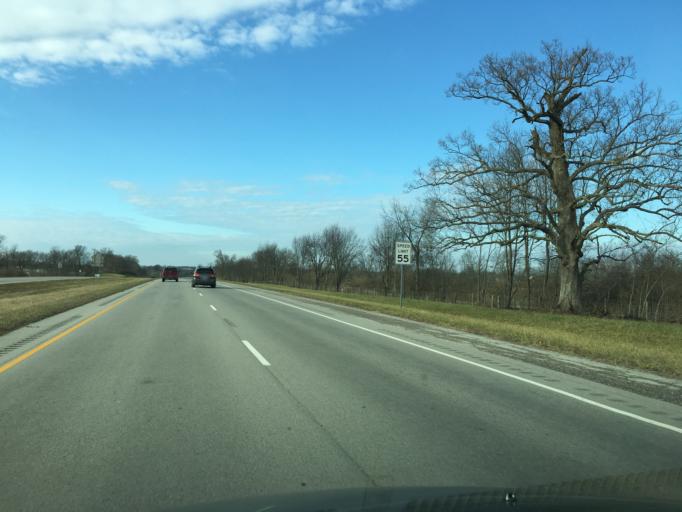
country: US
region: Kentucky
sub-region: Scott County
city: Georgetown
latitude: 38.1986
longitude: -84.5865
